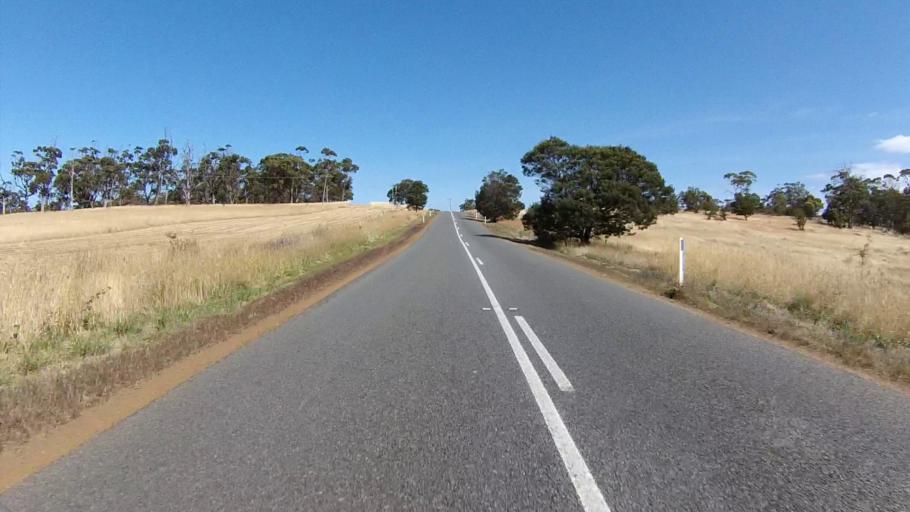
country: AU
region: Tasmania
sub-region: Sorell
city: Sorell
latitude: -42.2809
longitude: 147.9997
